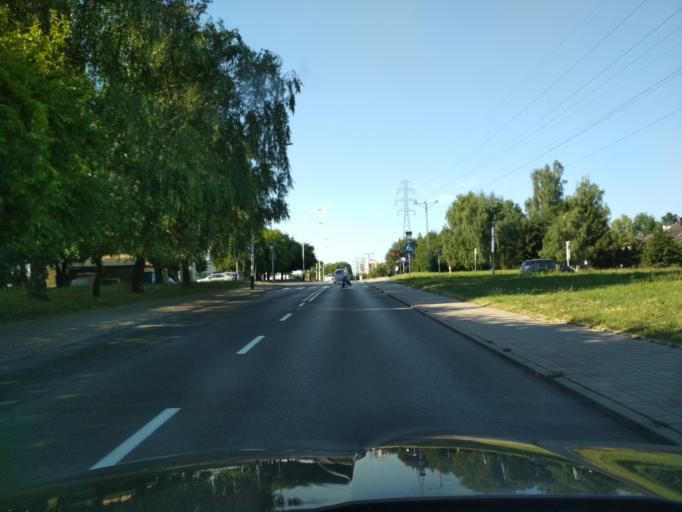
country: PL
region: Subcarpathian Voivodeship
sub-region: Rzeszow
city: Rzeszow
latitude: 50.0603
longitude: 21.9783
